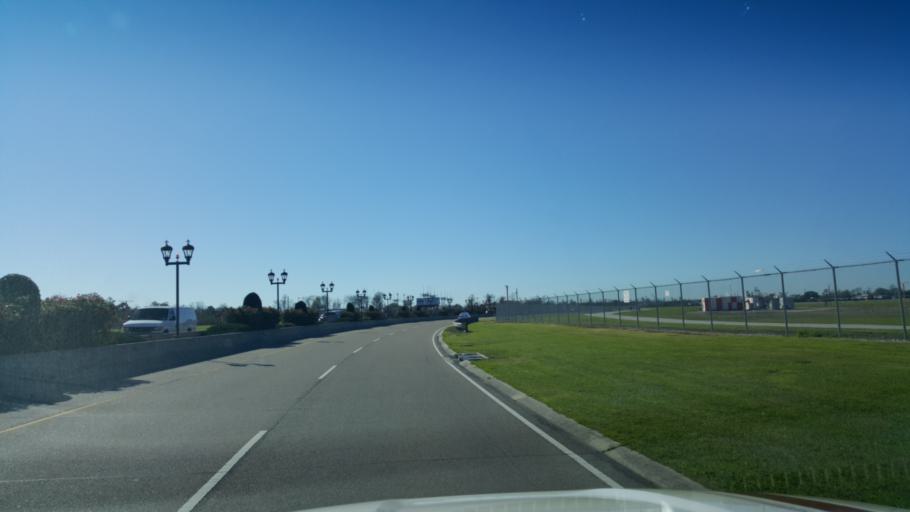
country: US
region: Louisiana
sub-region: Jefferson Parish
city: Kenner
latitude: 29.9898
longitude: -90.2479
